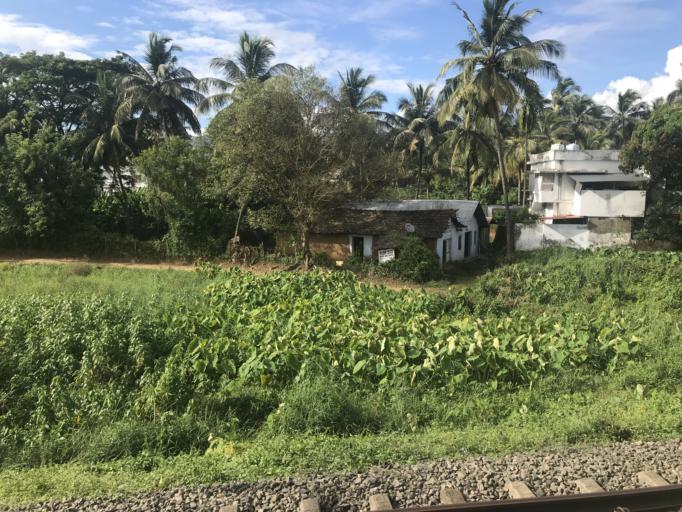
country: IN
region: Kerala
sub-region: Palakkad district
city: Palakkad
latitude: 10.8046
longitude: 76.6468
